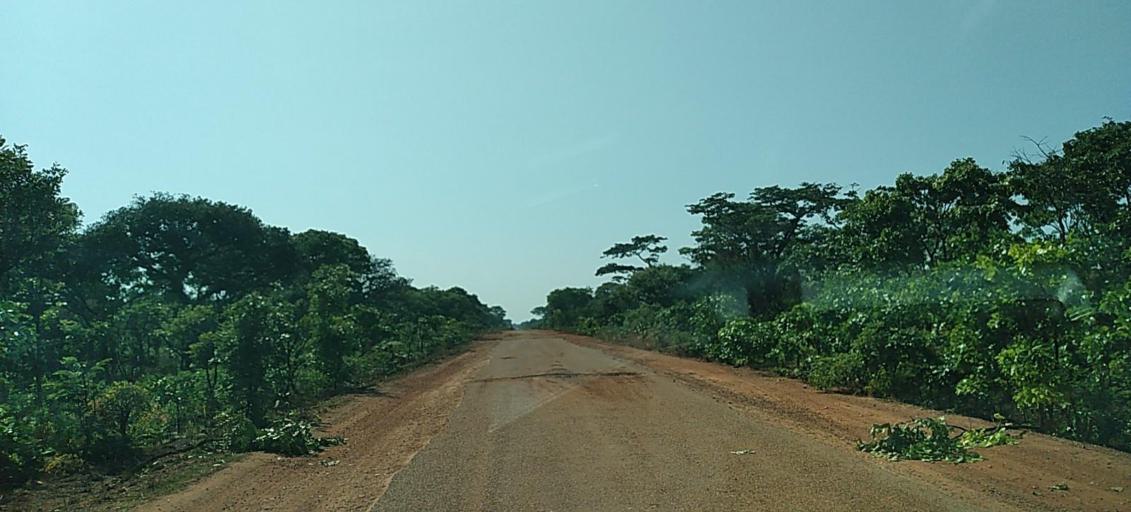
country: ZM
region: North-Western
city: Mwinilunga
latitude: -11.9091
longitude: 25.2946
